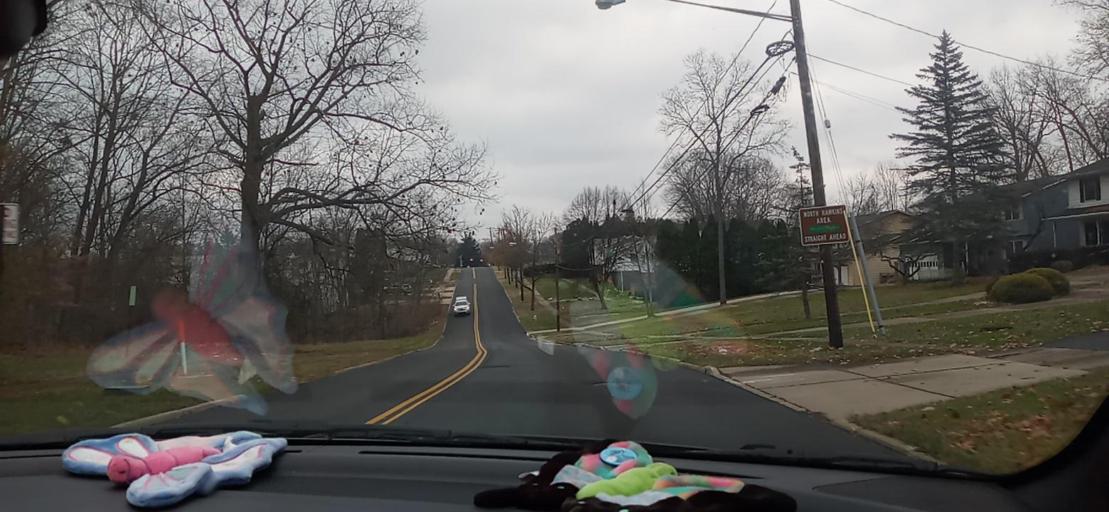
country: US
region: Ohio
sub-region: Summit County
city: Fairlawn
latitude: 41.1220
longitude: -81.5743
